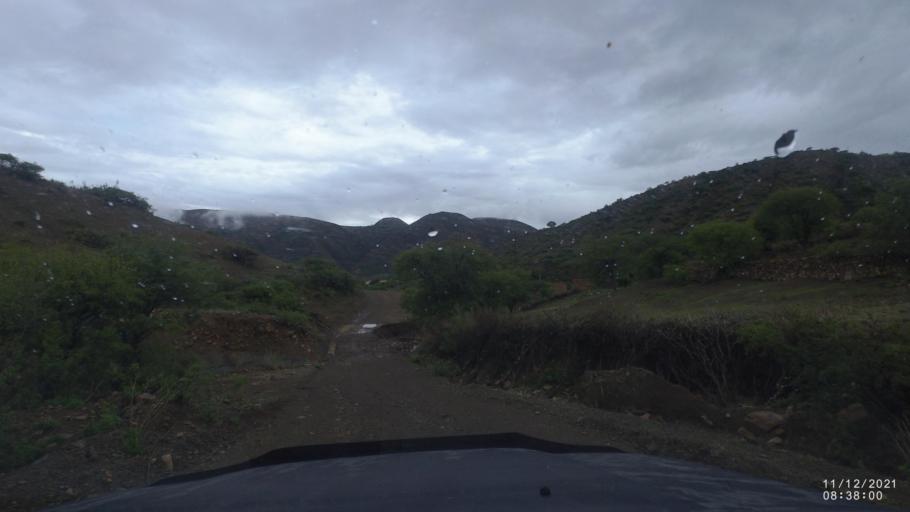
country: BO
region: Cochabamba
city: Tarata
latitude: -17.9242
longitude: -65.9366
